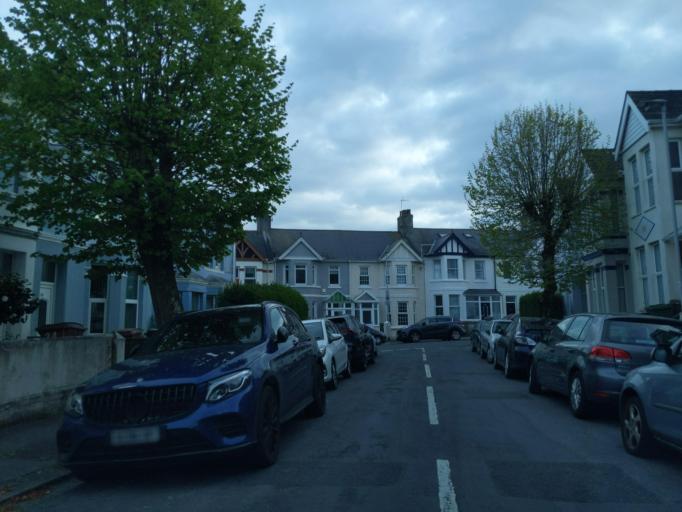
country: GB
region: England
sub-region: Plymouth
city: Plymouth
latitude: 50.3944
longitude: -4.1486
